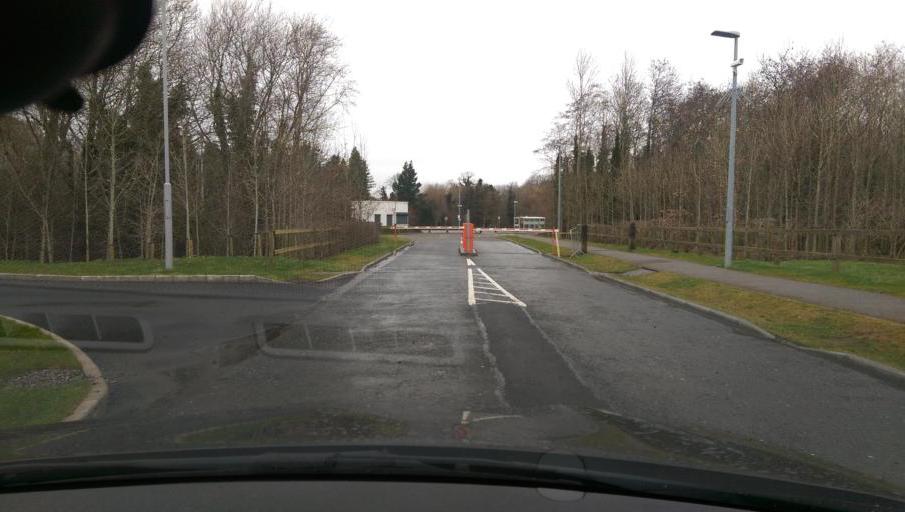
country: IE
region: Connaught
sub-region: County Galway
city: Gaillimh
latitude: 53.2894
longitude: -9.0705
